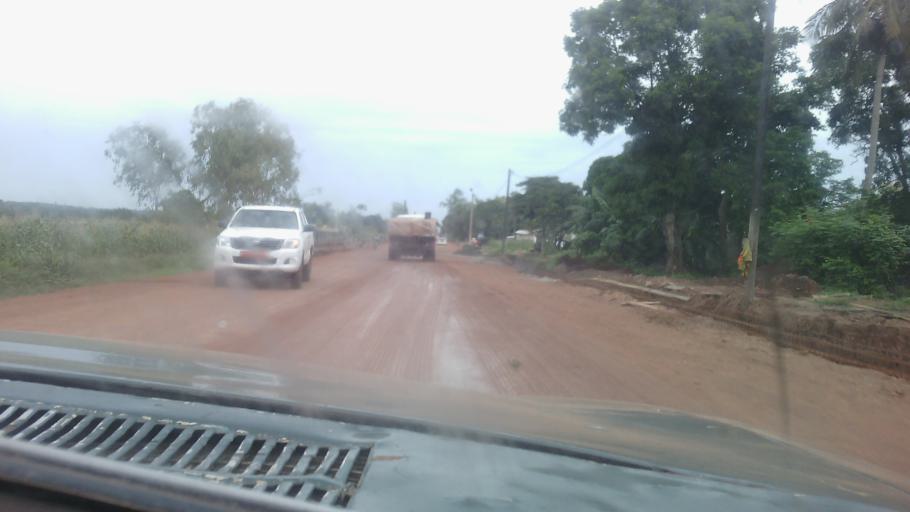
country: BJ
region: Mono
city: Lokossa
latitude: 6.5539
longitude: 1.8178
